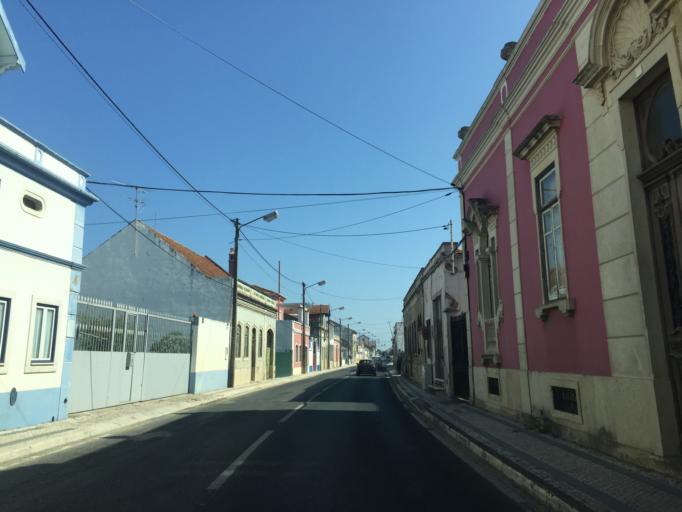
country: PT
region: Santarem
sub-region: Alpiarca
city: Alpiarca
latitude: 39.2625
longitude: -8.5820
